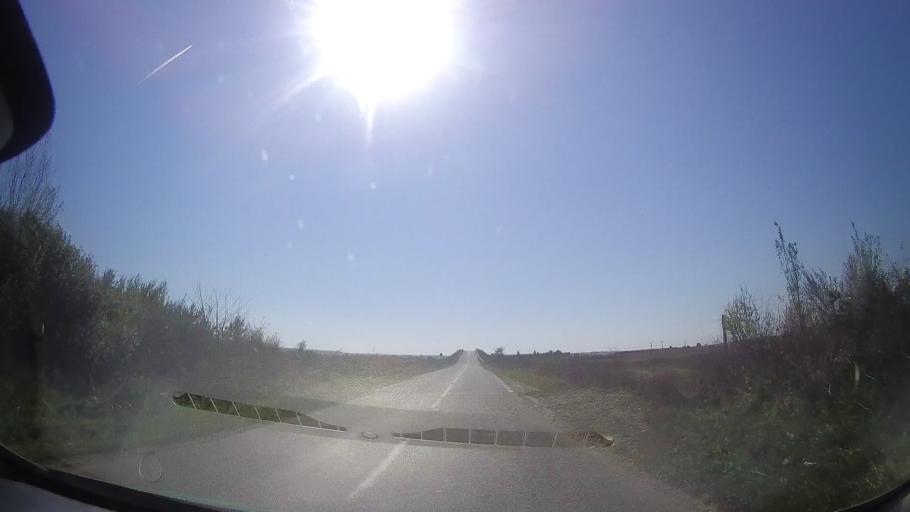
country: RO
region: Timis
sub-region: Comuna Bethausen
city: Bethausen
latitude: 45.8190
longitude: 21.9597
